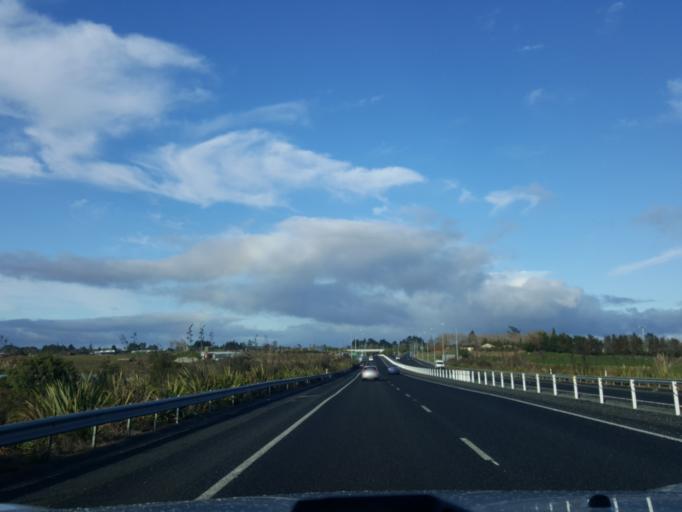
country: NZ
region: Waikato
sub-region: Waikato District
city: Ngaruawahia
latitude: -37.7011
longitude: 175.2102
